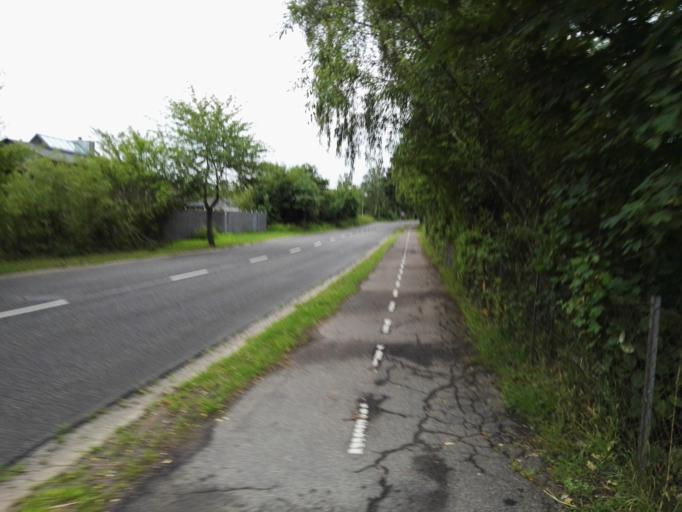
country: DK
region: Capital Region
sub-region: Egedal Kommune
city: Smorumnedre
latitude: 55.7450
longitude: 12.3101
